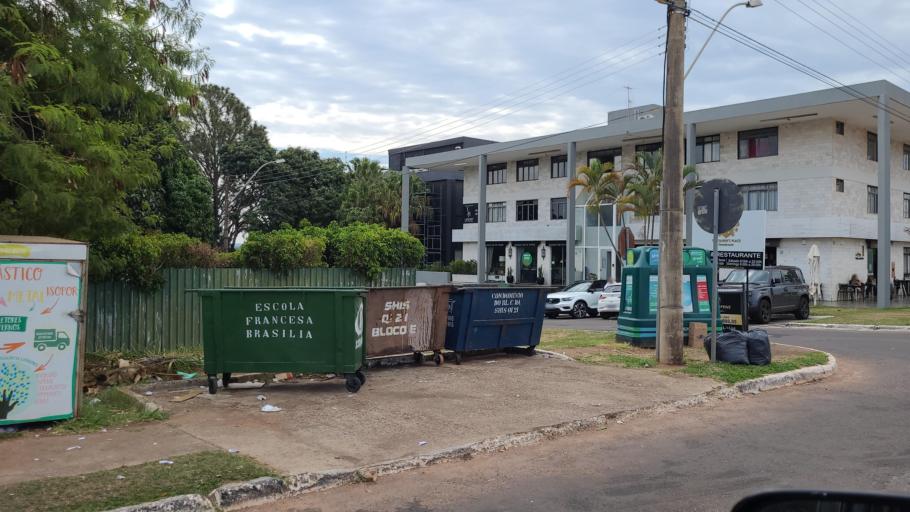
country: BR
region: Federal District
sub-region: Brasilia
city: Brasilia
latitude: -15.8555
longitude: -47.8532
